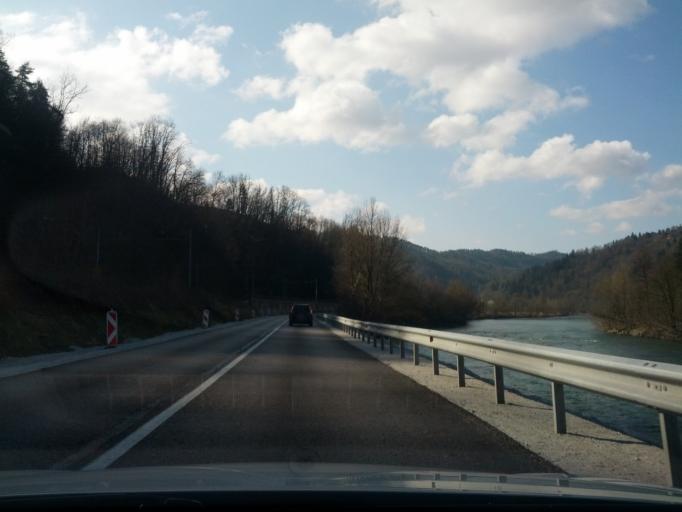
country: SI
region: Litija
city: Litija
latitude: 46.0723
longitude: 14.8220
